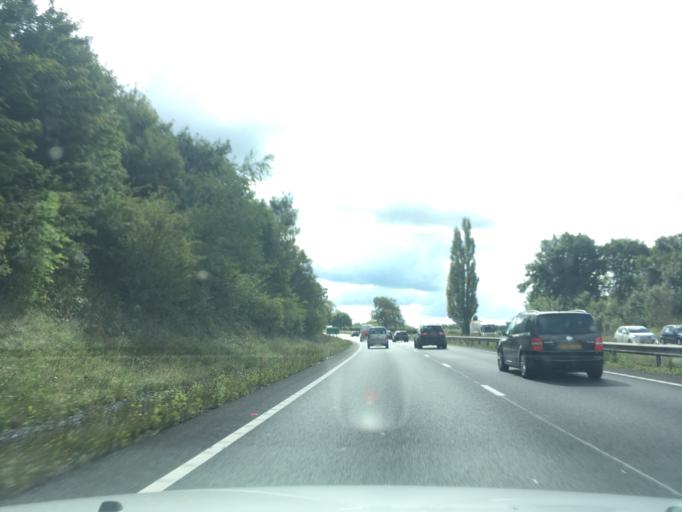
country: GB
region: England
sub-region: Surrey
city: Milford
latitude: 51.2065
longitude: -0.6507
